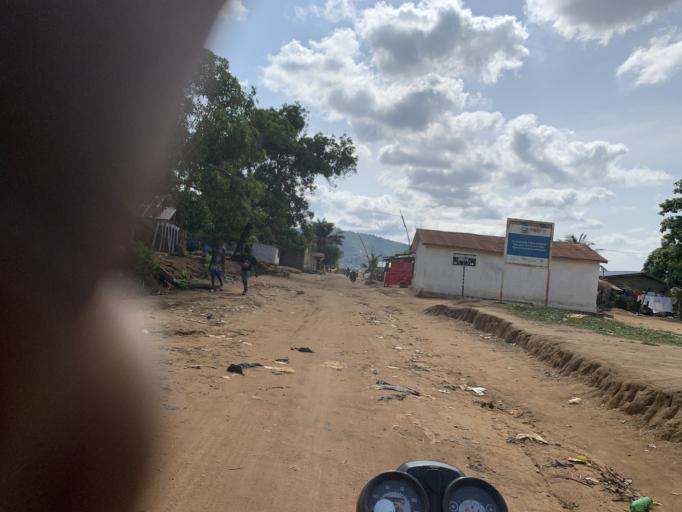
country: SL
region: Western Area
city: Waterloo
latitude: 8.3315
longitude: -13.0558
